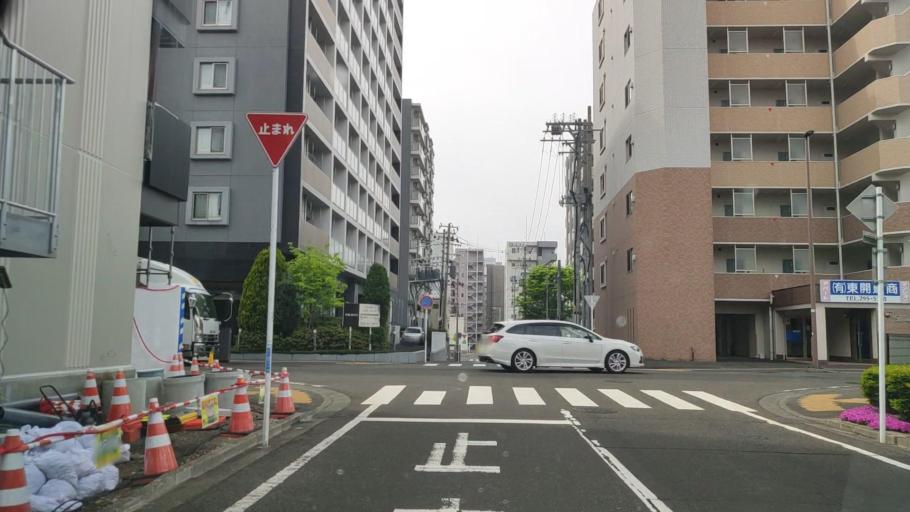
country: JP
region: Miyagi
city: Sendai-shi
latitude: 38.2639
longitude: 140.8884
